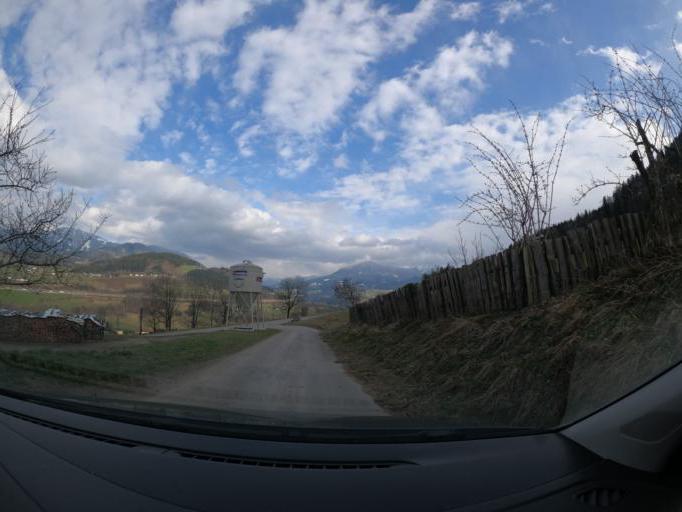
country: AT
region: Salzburg
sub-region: Politischer Bezirk Sankt Johann im Pongau
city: Pfarrwerfen
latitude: 47.4487
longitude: 13.1997
